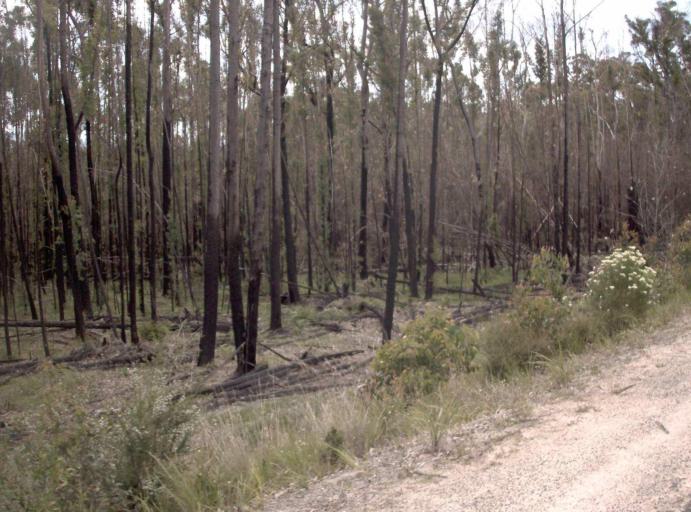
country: AU
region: New South Wales
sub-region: Bega Valley
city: Eden
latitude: -37.5408
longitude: 149.4624
